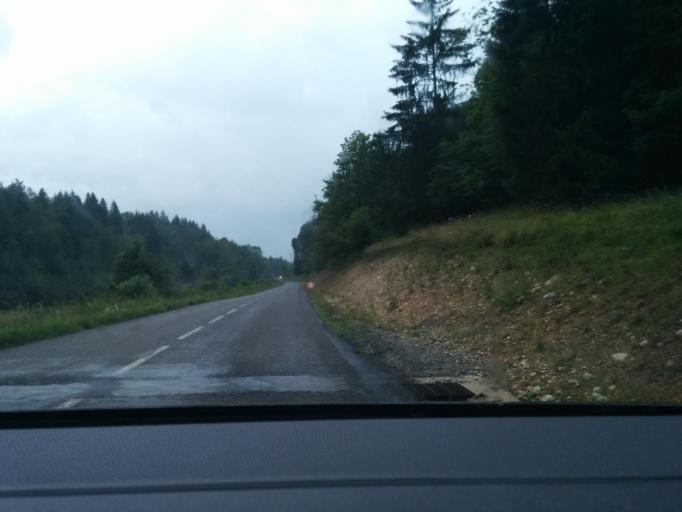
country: FR
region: Franche-Comte
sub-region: Departement du Jura
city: Valfin-les-Saint-Claude
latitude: 46.4465
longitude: 5.8240
